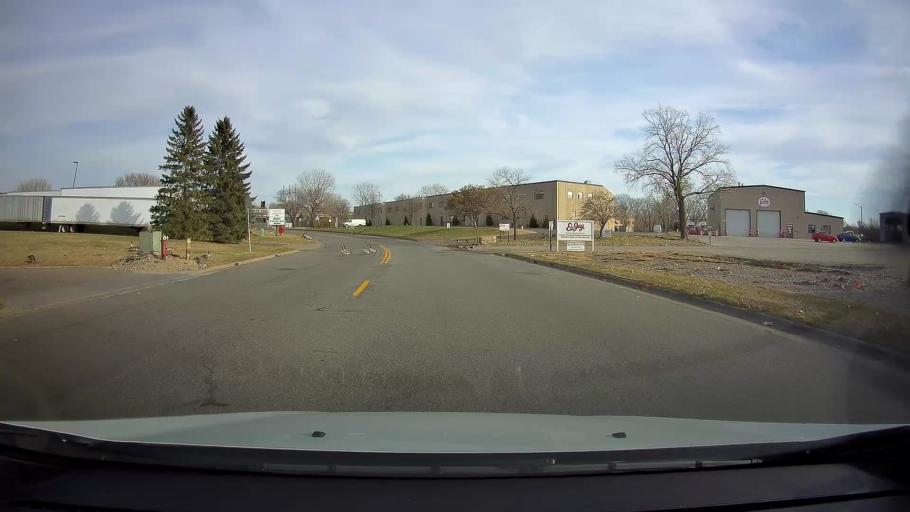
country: US
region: Minnesota
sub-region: Ramsey County
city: Lauderdale
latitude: 44.9773
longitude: -93.2081
